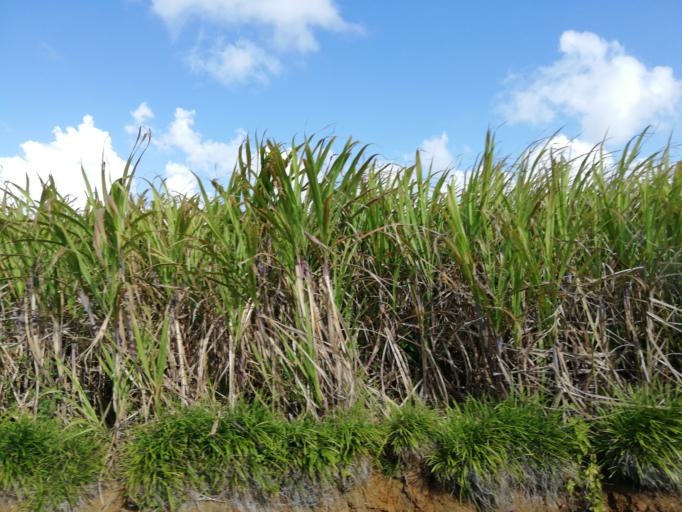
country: MU
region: Moka
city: Verdun
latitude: -20.2268
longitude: 57.5494
